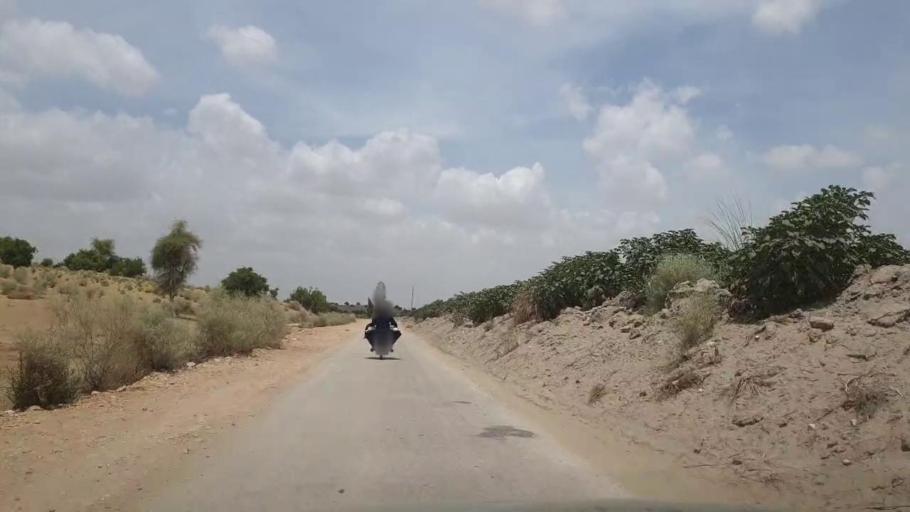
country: PK
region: Sindh
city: Kot Diji
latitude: 27.1990
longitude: 69.0810
